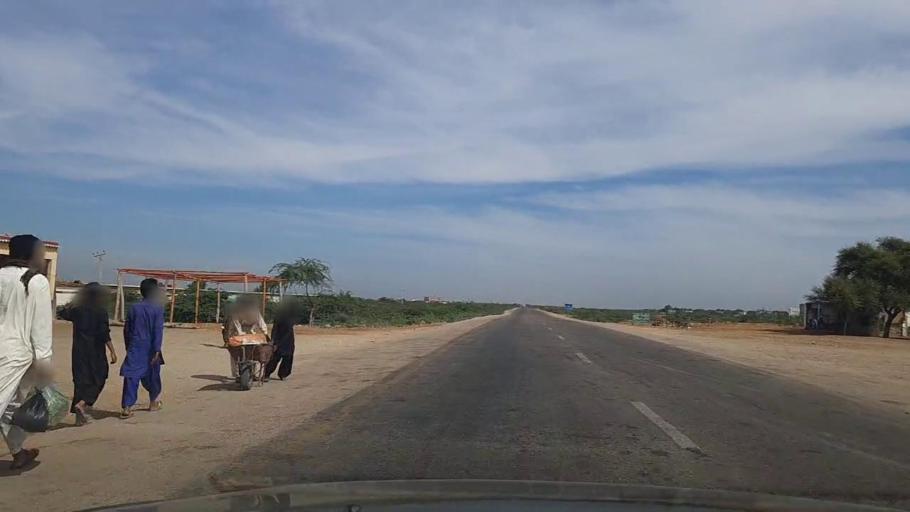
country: PK
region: Sindh
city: Thatta
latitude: 24.8364
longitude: 68.0012
